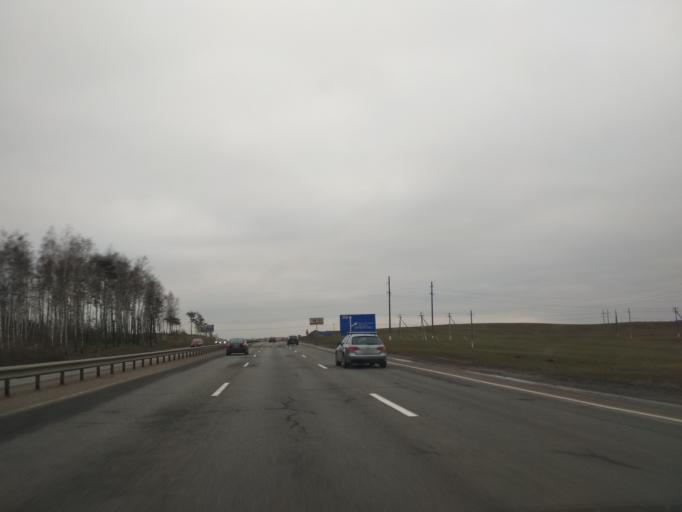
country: BY
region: Minsk
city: Pryvol'ny
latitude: 53.8160
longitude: 27.7709
